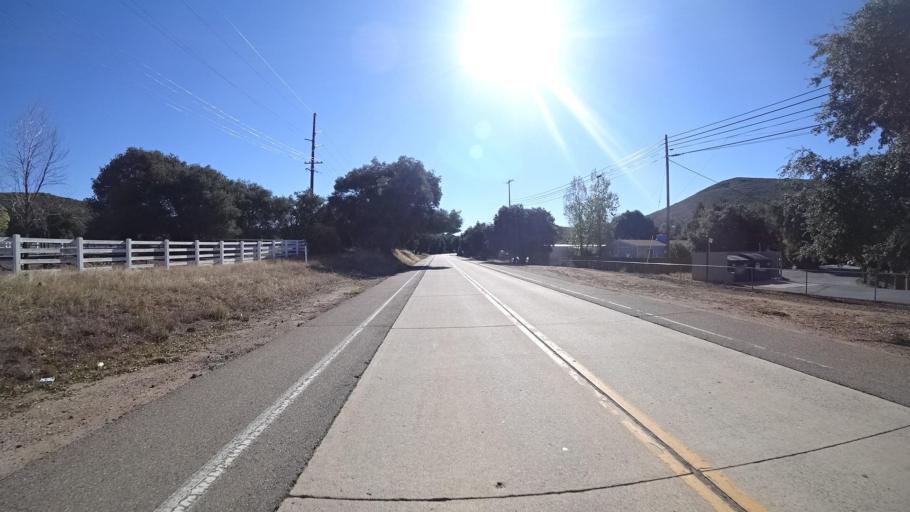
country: US
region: California
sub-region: San Diego County
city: Pine Valley
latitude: 32.8528
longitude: -116.5667
